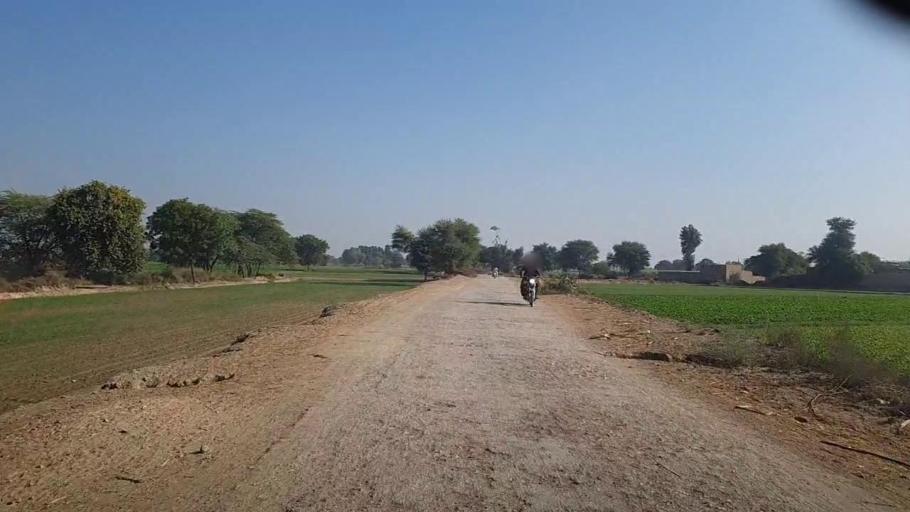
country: PK
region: Sindh
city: Darya Khan Marri
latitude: 26.6584
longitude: 68.3465
